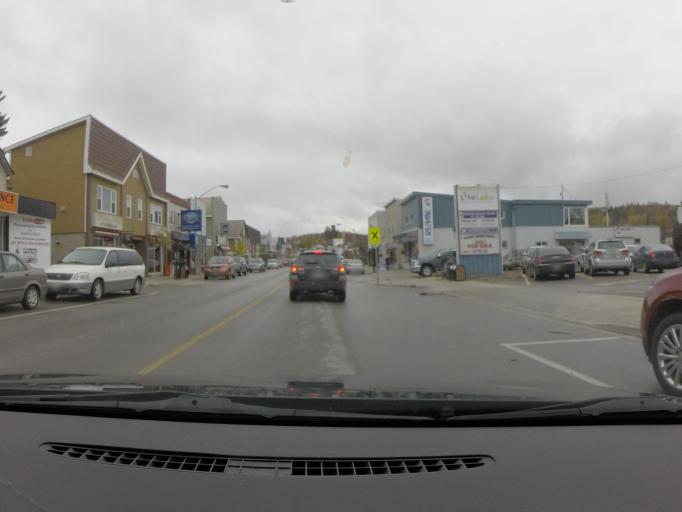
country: CA
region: Ontario
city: Bancroft
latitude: 45.0590
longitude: -77.8548
